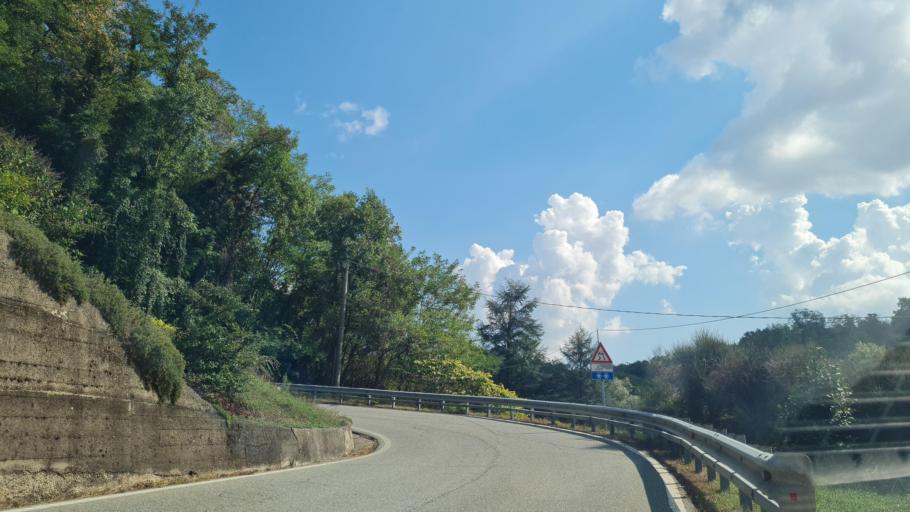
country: IT
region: Piedmont
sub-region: Provincia di Biella
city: Fontanella-Ozino
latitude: 45.6141
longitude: 8.1651
